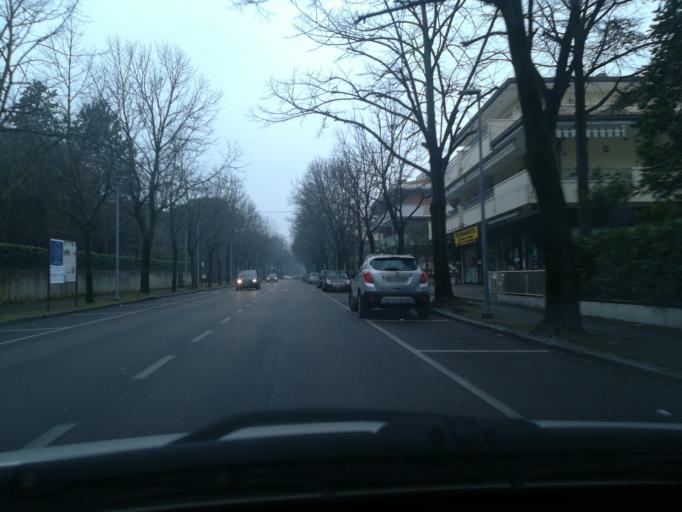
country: IT
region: Emilia-Romagna
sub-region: Provincia di Rimini
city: Riccione
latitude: 44.0060
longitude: 12.6465
